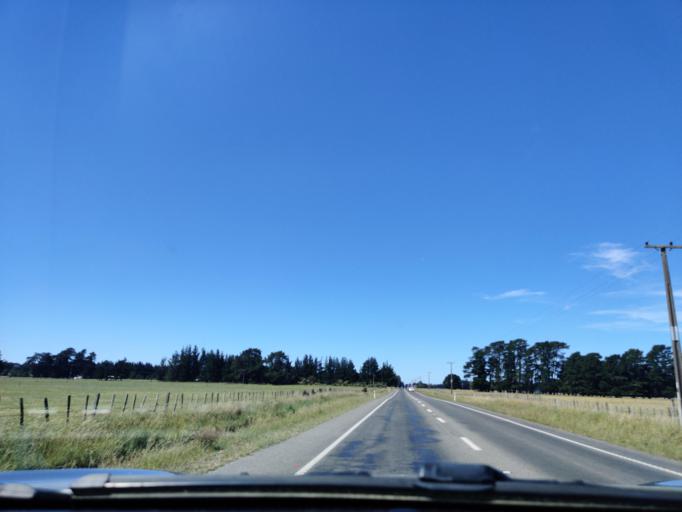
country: NZ
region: Wellington
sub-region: Masterton District
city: Masterton
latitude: -41.1035
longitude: 175.4156
